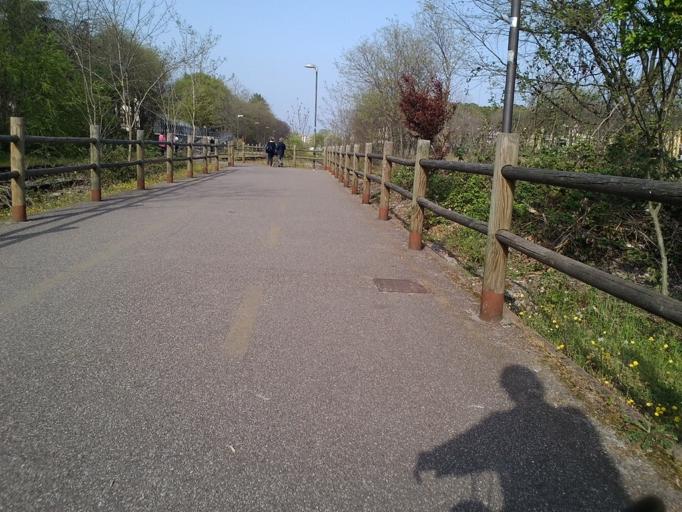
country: IT
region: Veneto
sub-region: Provincia di Verona
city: Verona
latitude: 45.4164
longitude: 10.9543
